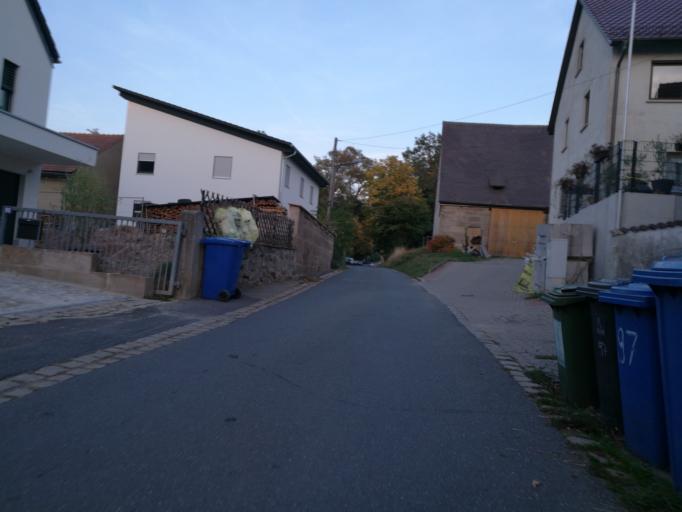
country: DE
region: Bavaria
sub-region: Regierungsbezirk Mittelfranken
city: Seukendorf
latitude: 49.4854
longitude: 10.9256
